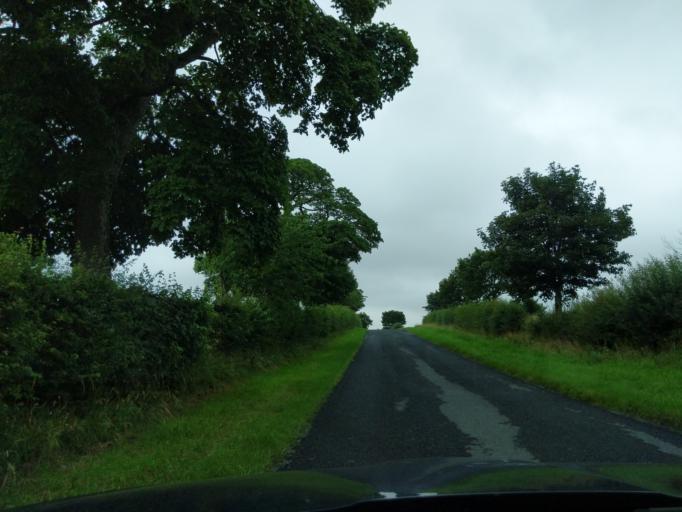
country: GB
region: England
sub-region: Northumberland
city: Ford
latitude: 55.6994
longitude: -2.1430
